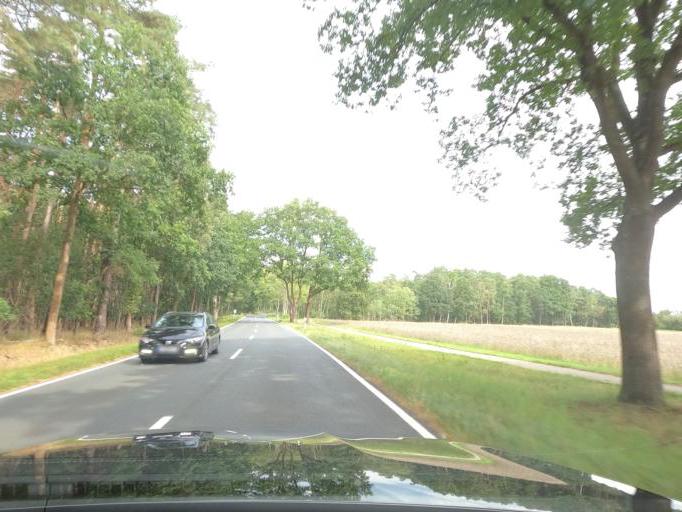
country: DE
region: Lower Saxony
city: Burgdorf
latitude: 52.5059
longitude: 9.9695
